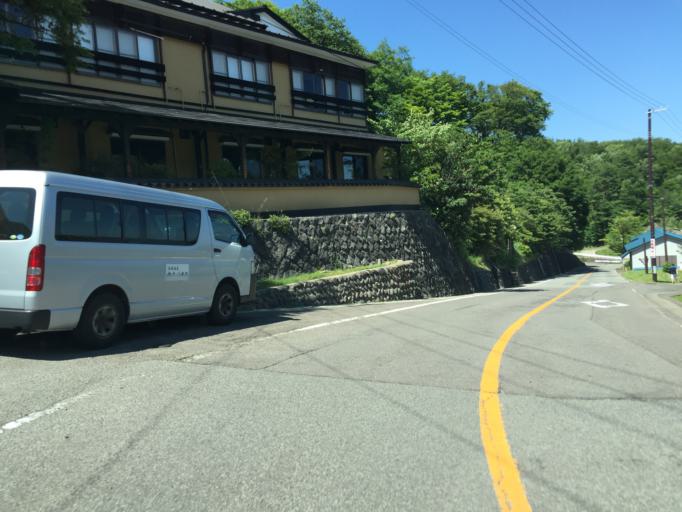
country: JP
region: Fukushima
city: Fukushima-shi
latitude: 37.7525
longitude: 140.3046
